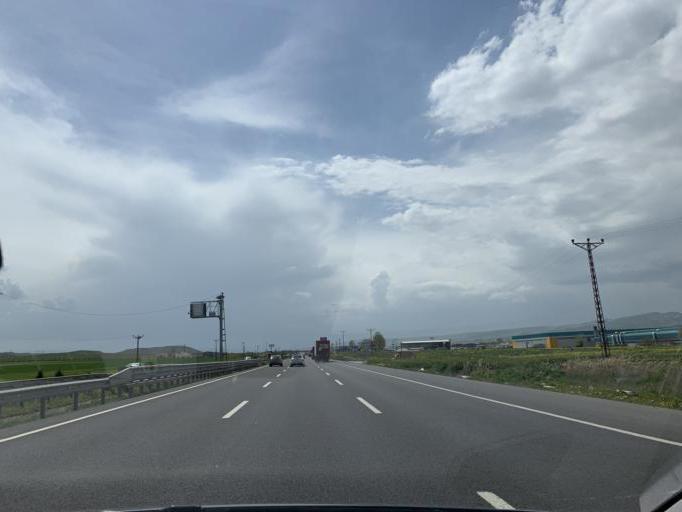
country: TR
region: Ankara
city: Temelli
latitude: 39.7216
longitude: 32.3381
